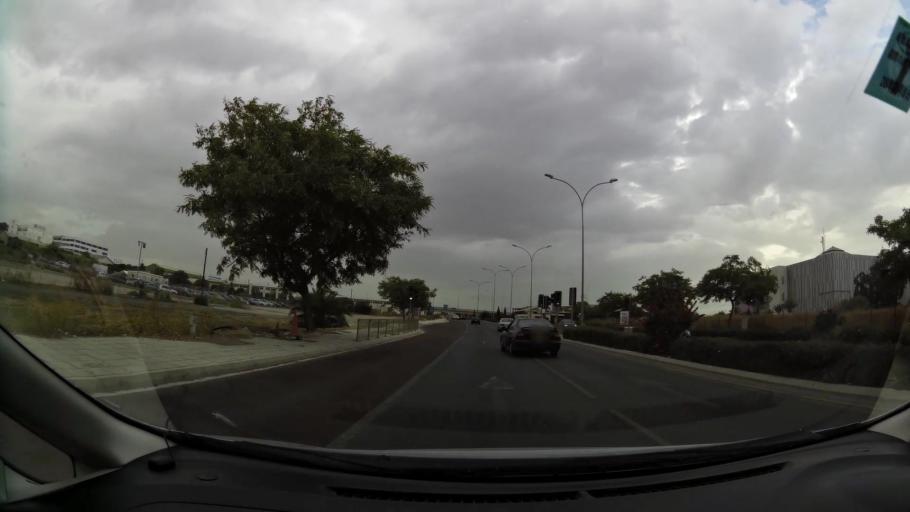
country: CY
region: Lefkosia
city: Nicosia
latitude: 35.1267
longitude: 33.3688
